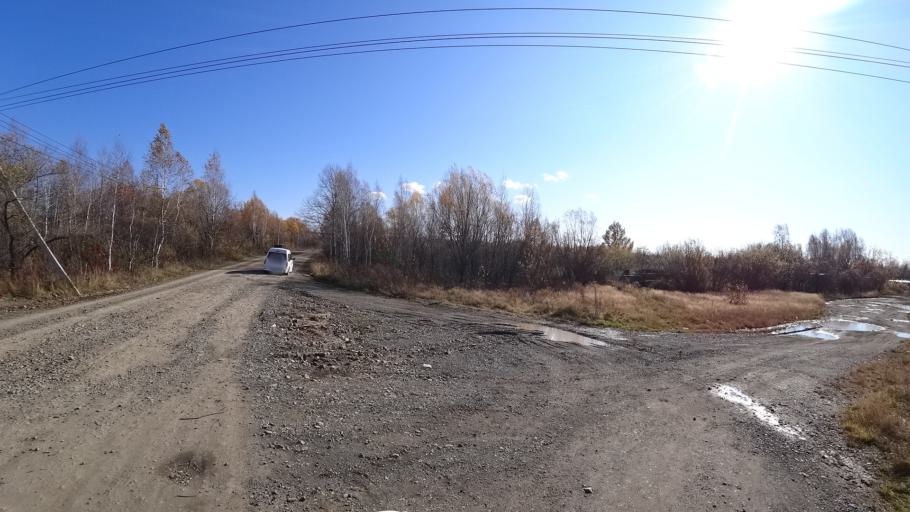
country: RU
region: Khabarovsk Krai
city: Amursk
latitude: 50.1050
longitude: 136.5216
